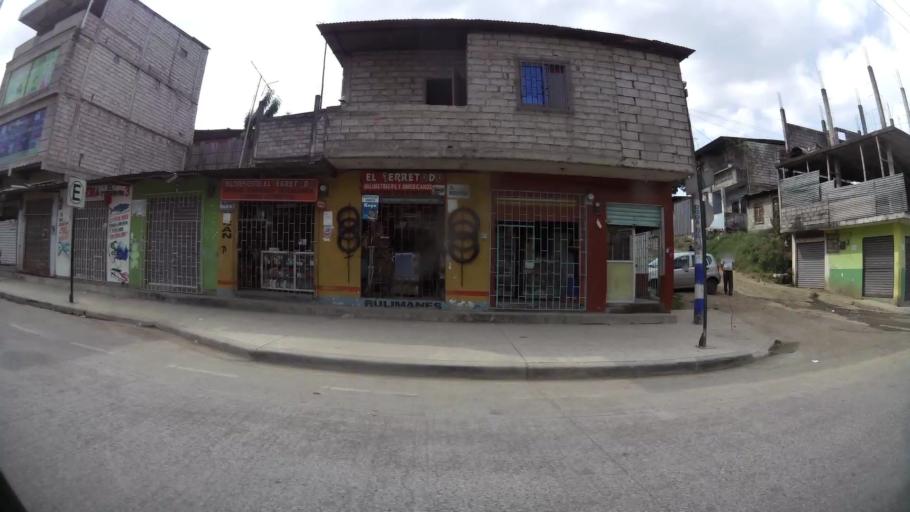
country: EC
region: Guayas
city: Santa Lucia
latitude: -2.1194
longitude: -79.9527
